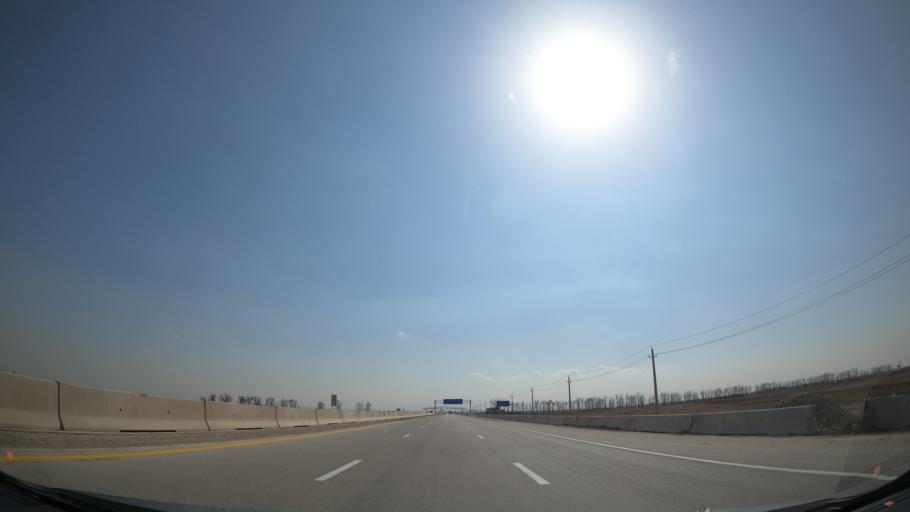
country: IR
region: Qazvin
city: Abyek
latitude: 35.9645
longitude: 50.4626
